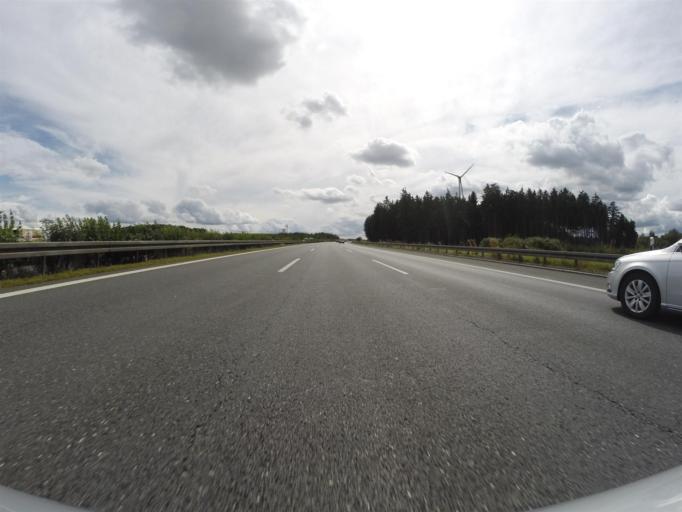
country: DE
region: Bavaria
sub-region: Upper Franconia
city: Leupoldsgrun
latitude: 50.2521
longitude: 11.7928
